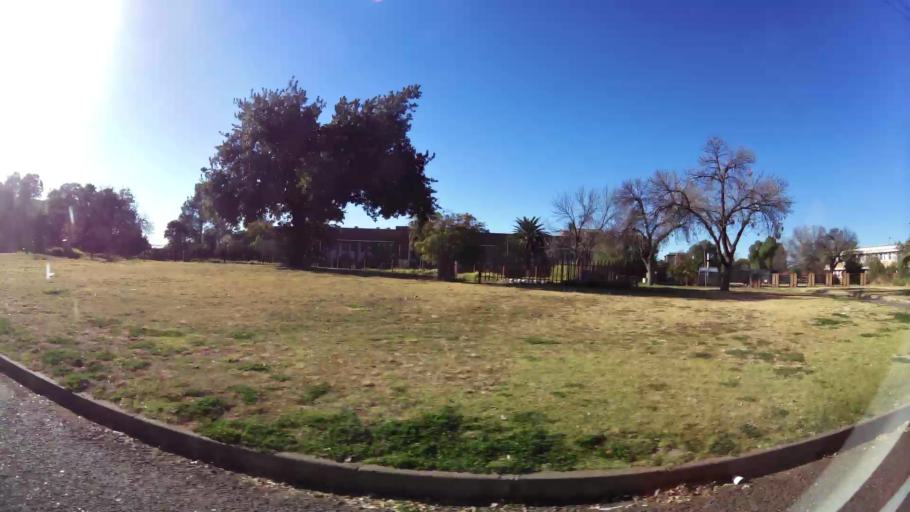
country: ZA
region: Northern Cape
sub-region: Frances Baard District Municipality
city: Kimberley
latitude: -28.7446
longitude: 24.7681
